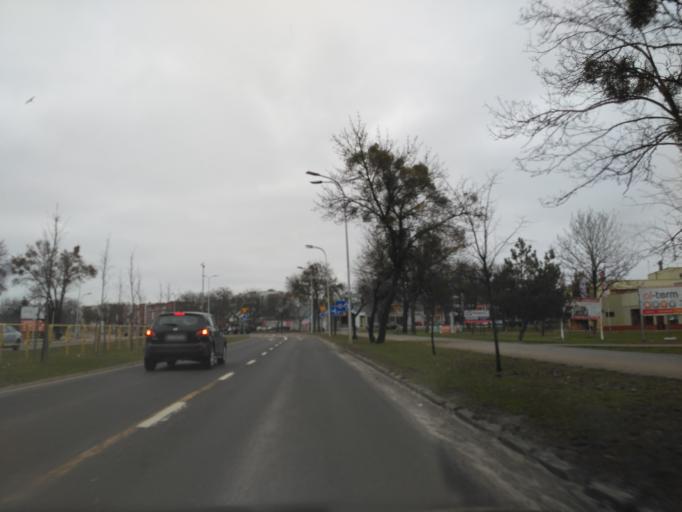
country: PL
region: Lublin Voivodeship
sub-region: Chelm
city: Chelm
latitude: 51.1277
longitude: 23.4802
